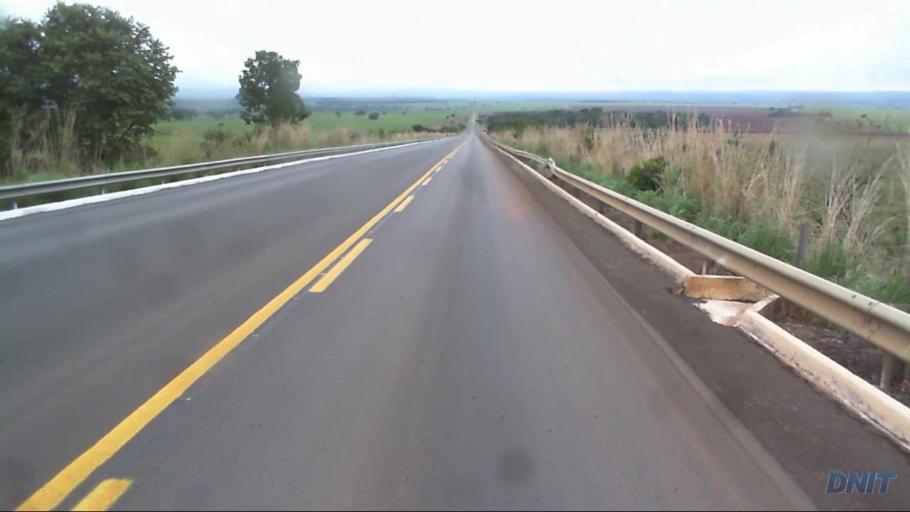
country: BR
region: Goias
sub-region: Padre Bernardo
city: Padre Bernardo
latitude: -15.1773
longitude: -48.4125
